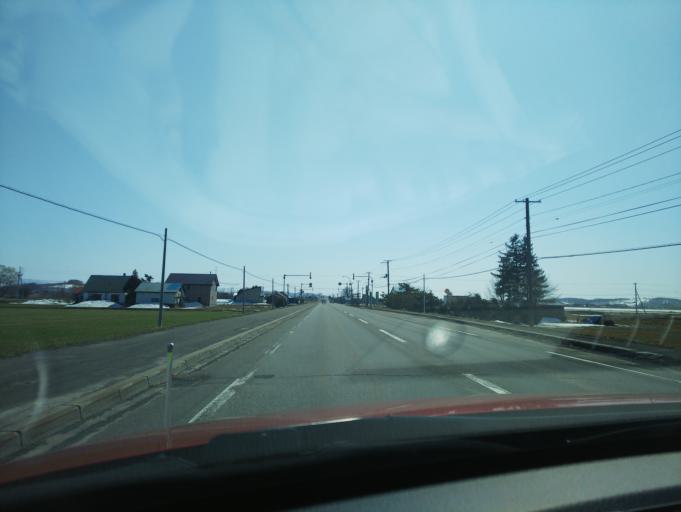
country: JP
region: Hokkaido
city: Nayoro
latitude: 44.2020
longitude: 142.3949
